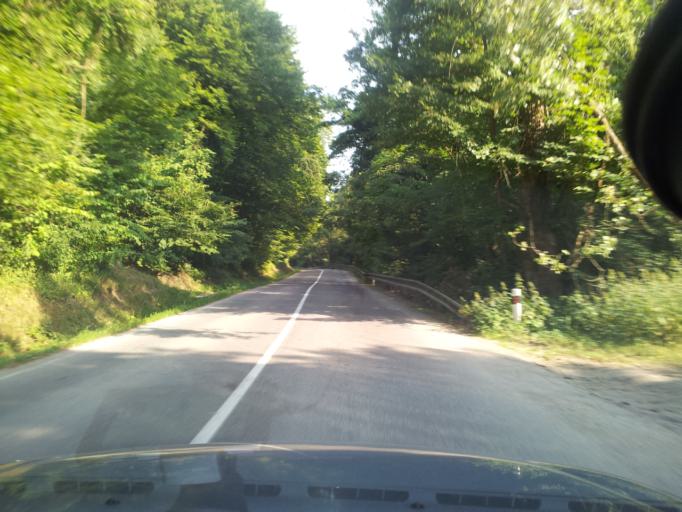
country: SK
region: Nitriansky
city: Trencianske Teplice
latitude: 48.8980
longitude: 18.1690
